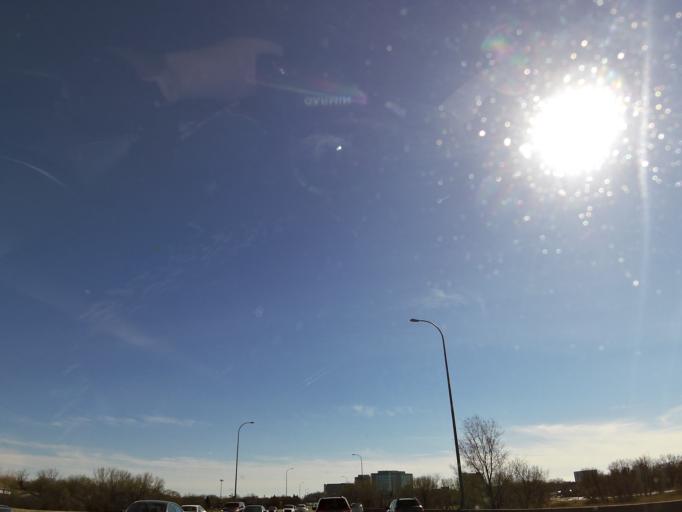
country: US
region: Minnesota
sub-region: Hennepin County
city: Minnetonka Mills
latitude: 44.9082
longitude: -93.4014
